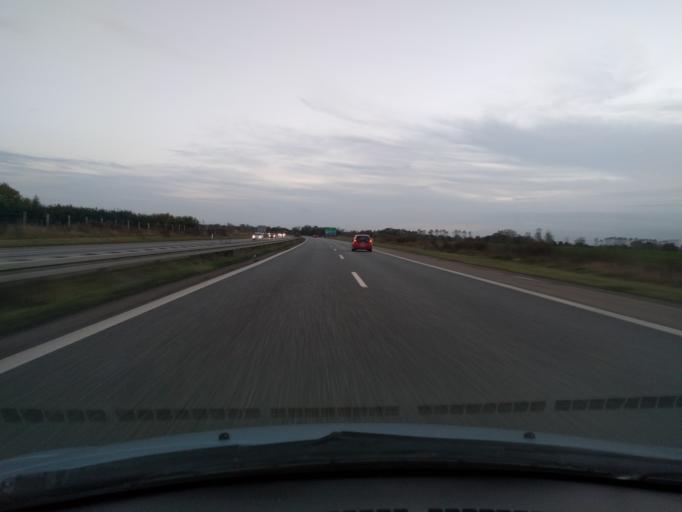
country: DK
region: South Denmark
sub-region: Faaborg-Midtfyn Kommune
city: Arslev
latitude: 55.2991
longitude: 10.4373
